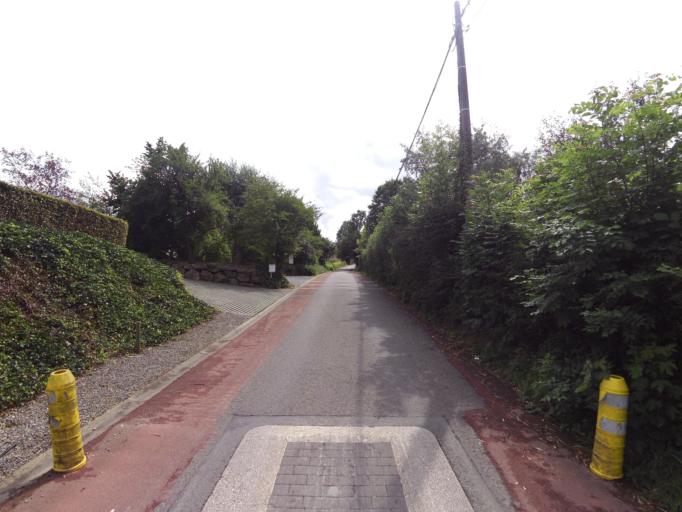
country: BE
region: Wallonia
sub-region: Province de Liege
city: Tinlot
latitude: 50.5103
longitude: 5.3649
